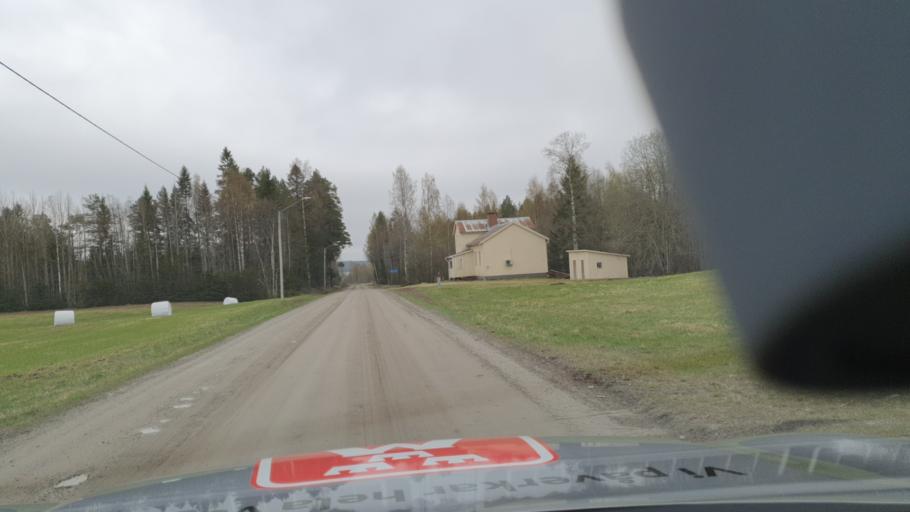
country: SE
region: Vaesterbotten
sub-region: Bjurholms Kommun
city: Bjurholm
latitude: 63.6493
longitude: 19.0486
